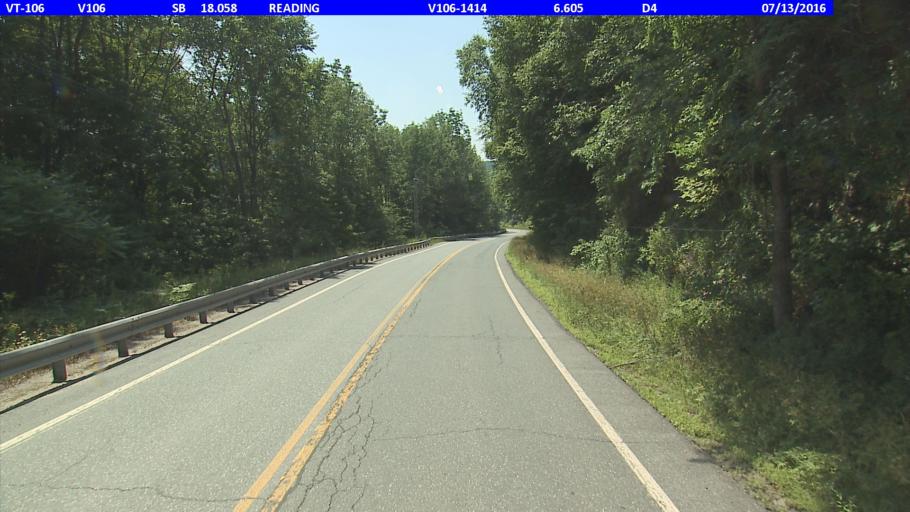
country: US
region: Vermont
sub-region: Windsor County
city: Woodstock
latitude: 43.5294
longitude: -72.5554
